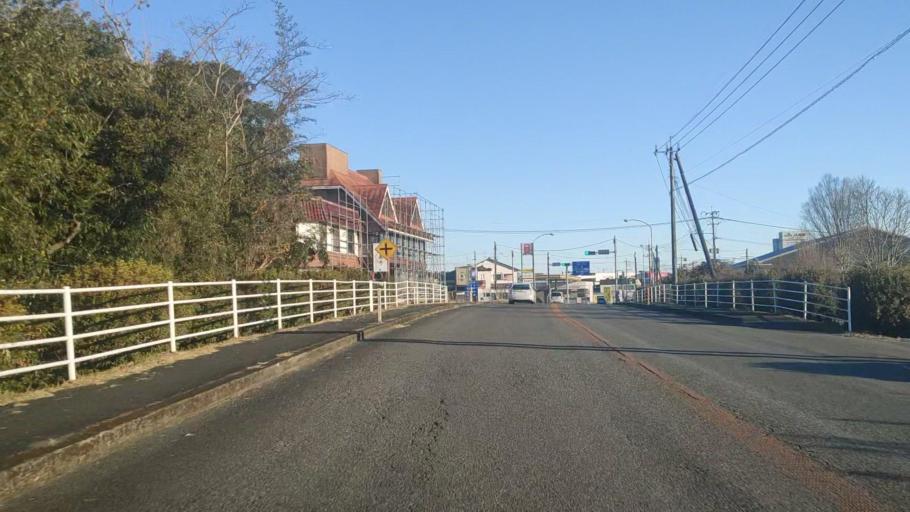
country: JP
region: Miyazaki
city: Takanabe
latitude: 32.1949
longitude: 131.5247
